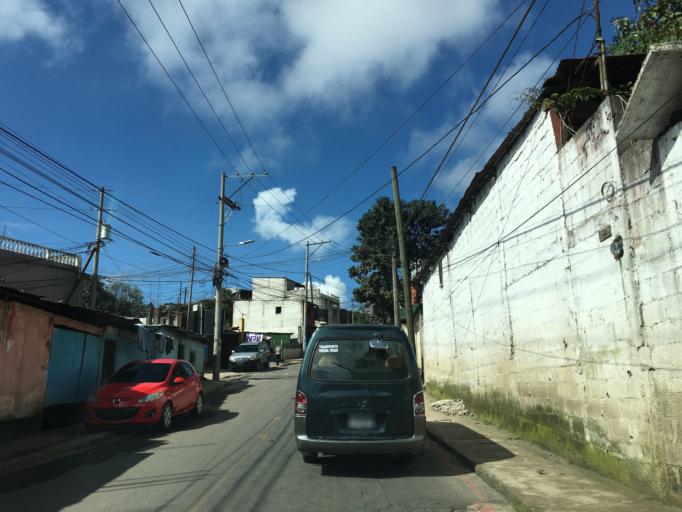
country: GT
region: Guatemala
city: San Jose Pinula
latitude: 14.5539
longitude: -90.4381
